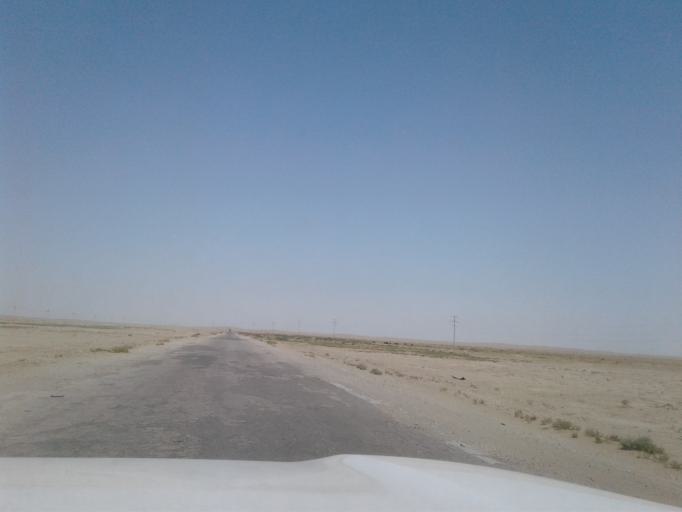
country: TM
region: Balkan
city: Gumdag
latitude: 38.3515
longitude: 54.3709
